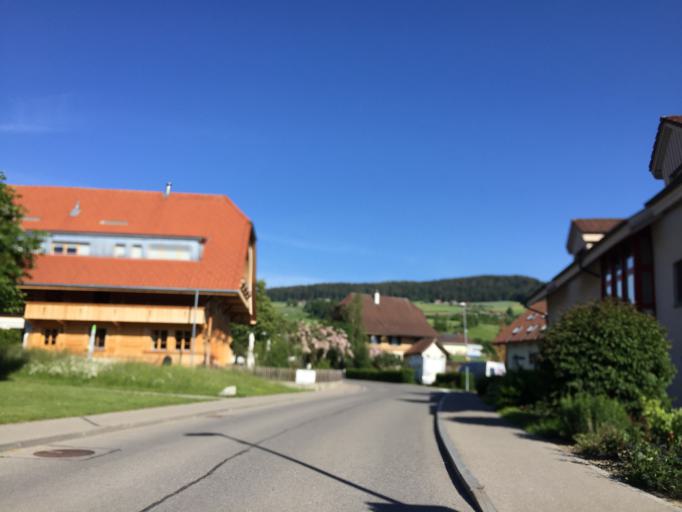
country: CH
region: Bern
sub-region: Bern-Mittelland District
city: Konolfingen
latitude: 46.8714
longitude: 7.6243
